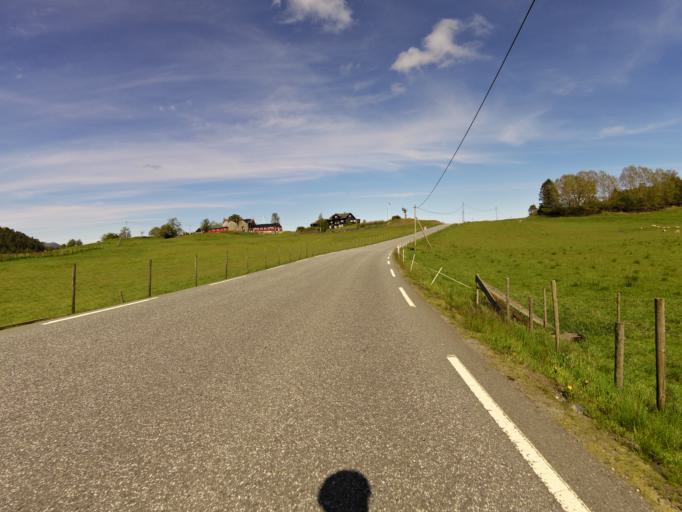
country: NO
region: Hordaland
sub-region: Stord
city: Leirvik
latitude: 59.7878
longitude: 5.4659
